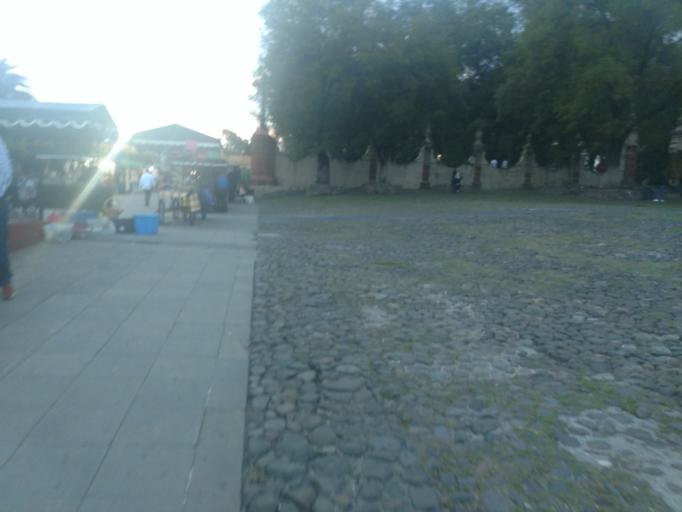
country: MX
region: Mexico
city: Tepotzotlan
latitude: 19.7132
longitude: -99.2228
